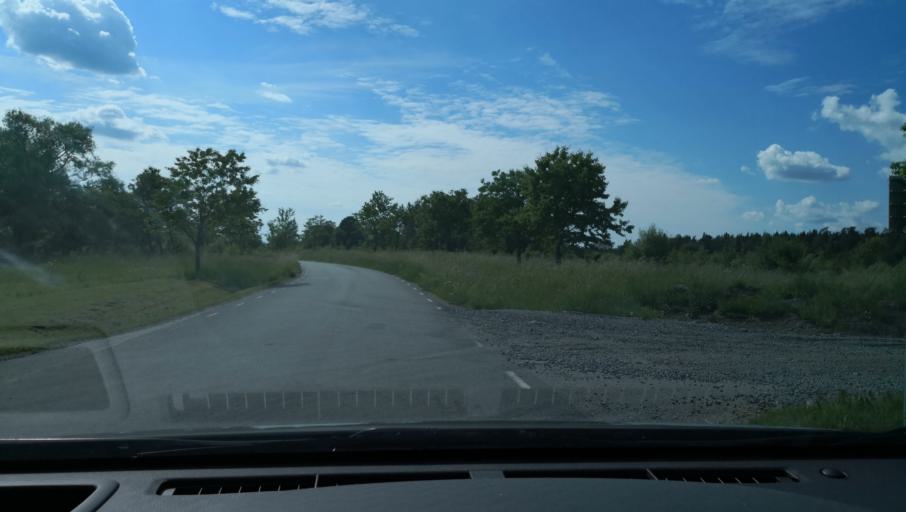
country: SE
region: Uppsala
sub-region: Enkopings Kommun
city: Orsundsbro
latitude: 59.8163
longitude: 17.3667
